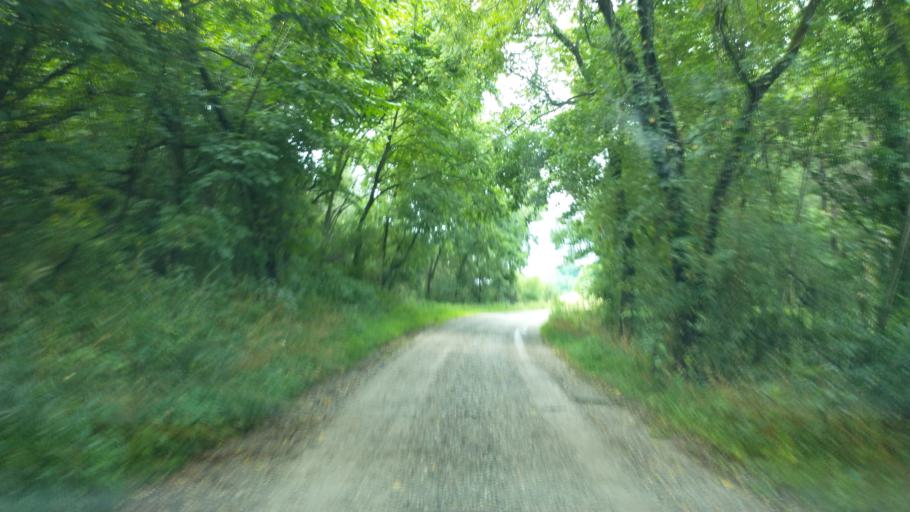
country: US
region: Ohio
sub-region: Meigs County
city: Middleport
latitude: 38.9251
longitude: -82.0543
